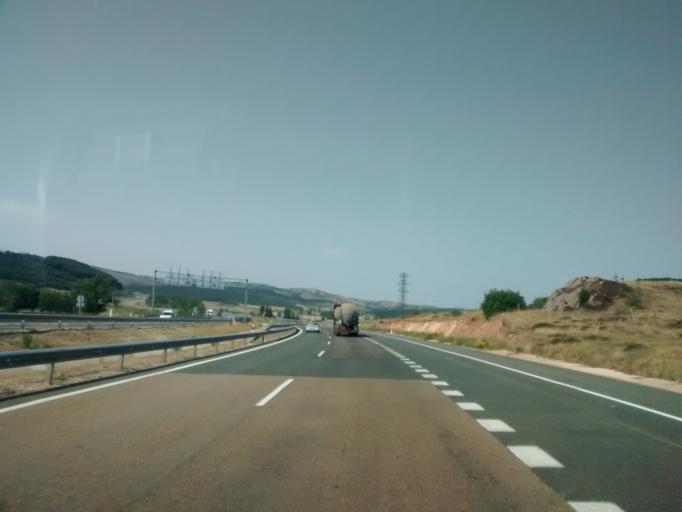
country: ES
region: Castille and Leon
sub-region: Provincia de Palencia
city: Aguilar de Campoo
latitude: 42.7693
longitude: -4.2767
